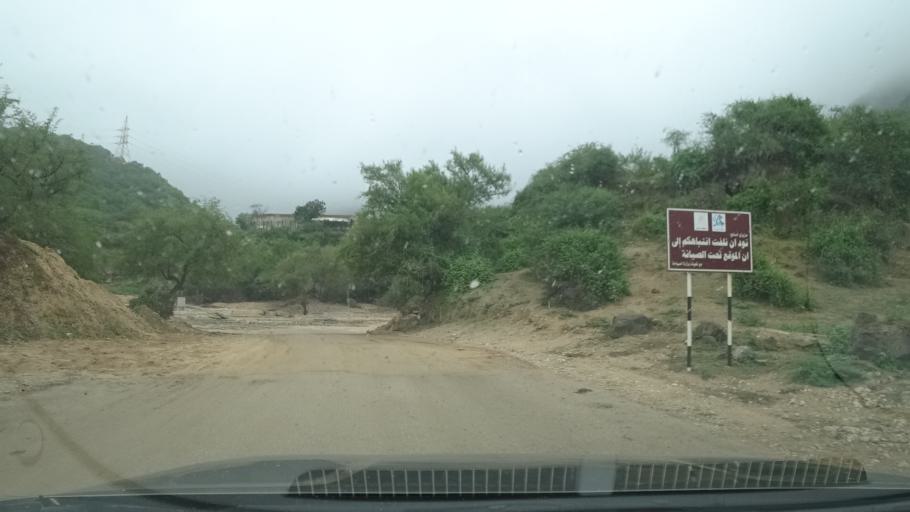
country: OM
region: Zufar
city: Salalah
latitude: 17.1053
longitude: 54.0753
